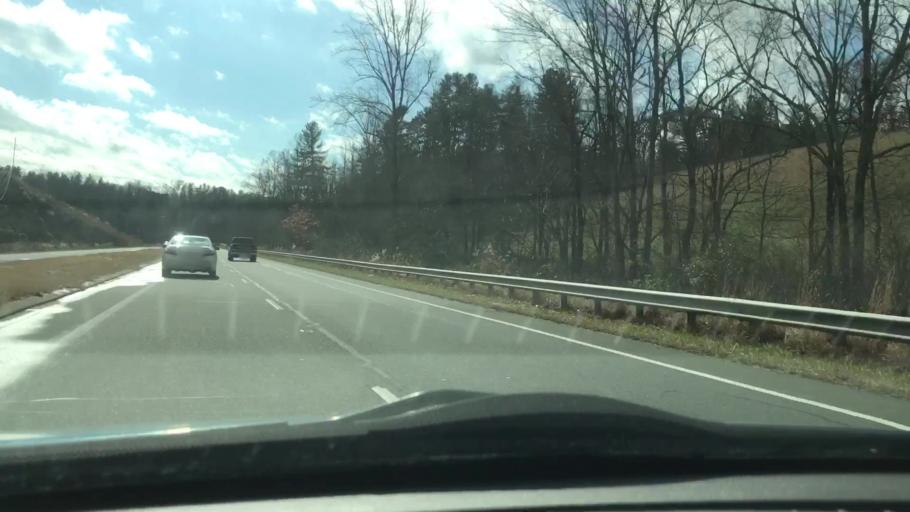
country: US
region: North Carolina
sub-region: Madison County
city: Mars Hill
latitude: 35.8588
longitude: -82.4869
